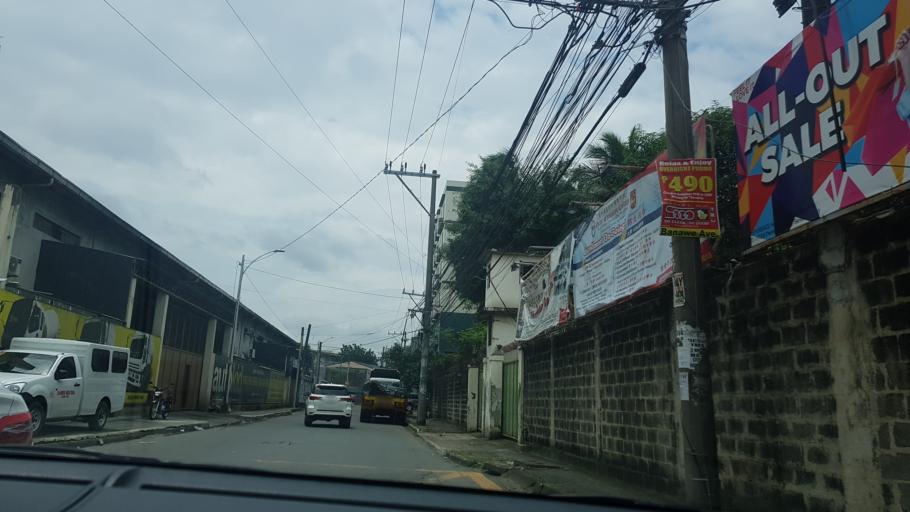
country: PH
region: Calabarzon
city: Del Monte
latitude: 14.6514
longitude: 121.0035
